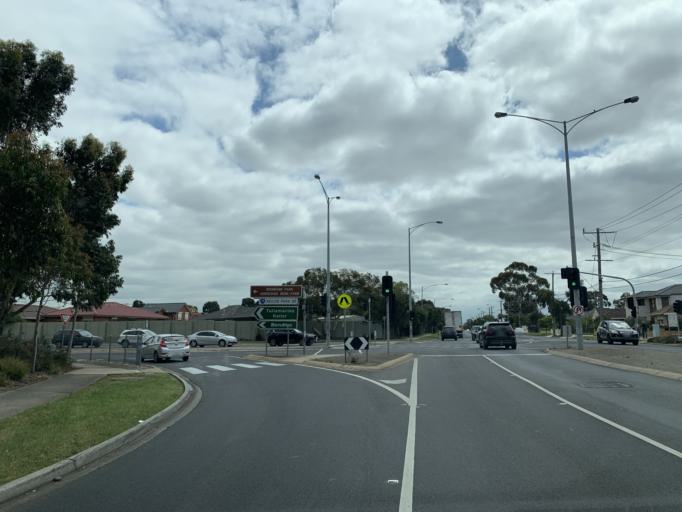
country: AU
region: Victoria
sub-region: Moonee Valley
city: Keilor East
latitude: -37.7402
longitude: 144.8636
